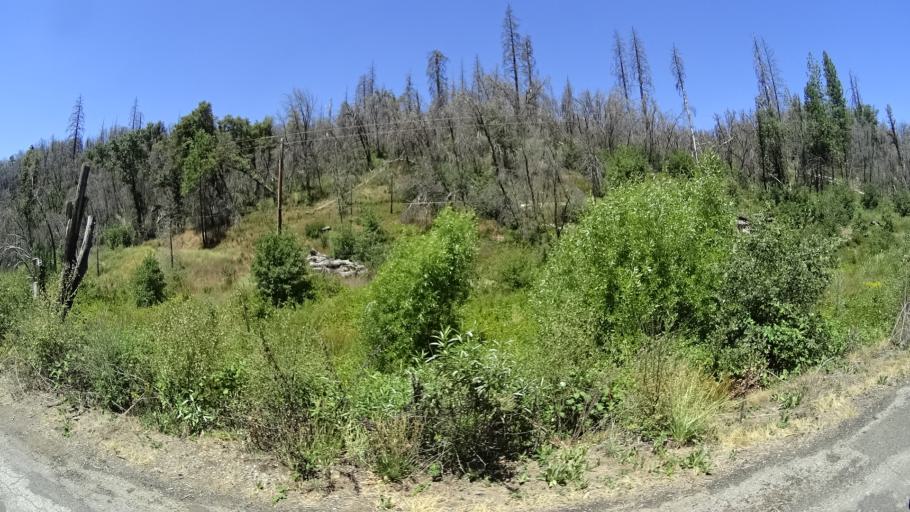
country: US
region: California
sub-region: Calaveras County
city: Mountain Ranch
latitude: 38.2503
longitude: -120.5269
